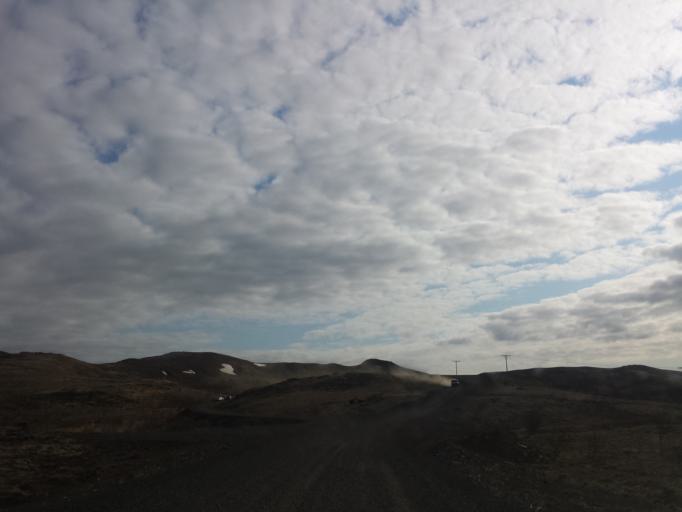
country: IS
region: Capital Region
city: Mosfellsbaer
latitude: 64.0725
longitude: -21.6547
